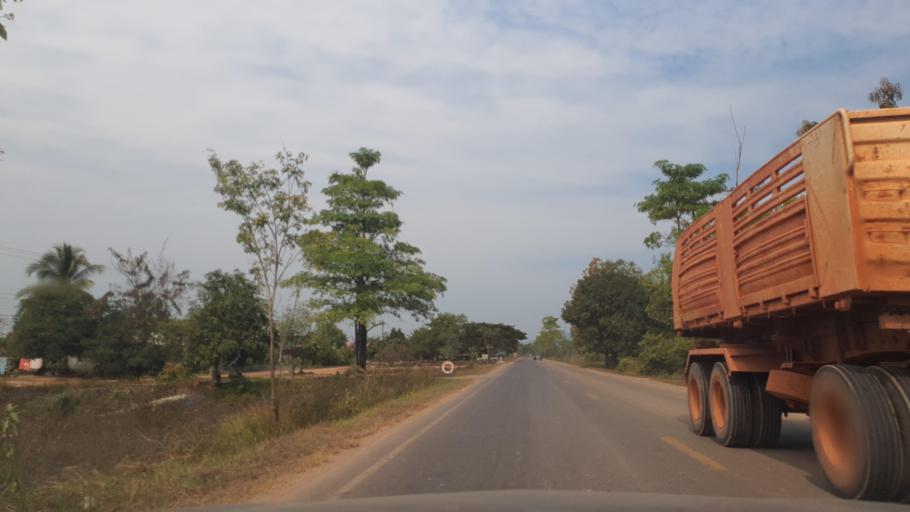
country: TH
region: Changwat Bueng Kan
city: Bung Khla
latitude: 18.1957
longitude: 104.0534
